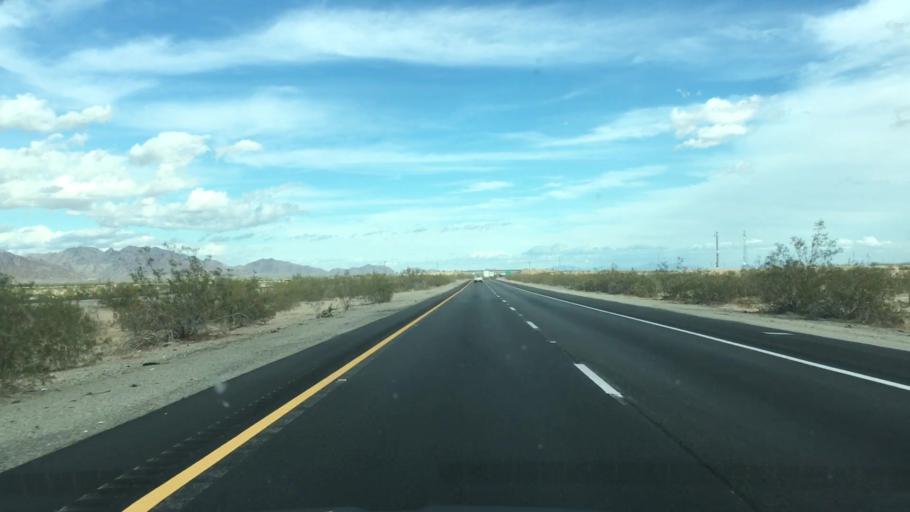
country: US
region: California
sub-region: Riverside County
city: Mesa Verde
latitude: 33.6069
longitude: -114.9135
